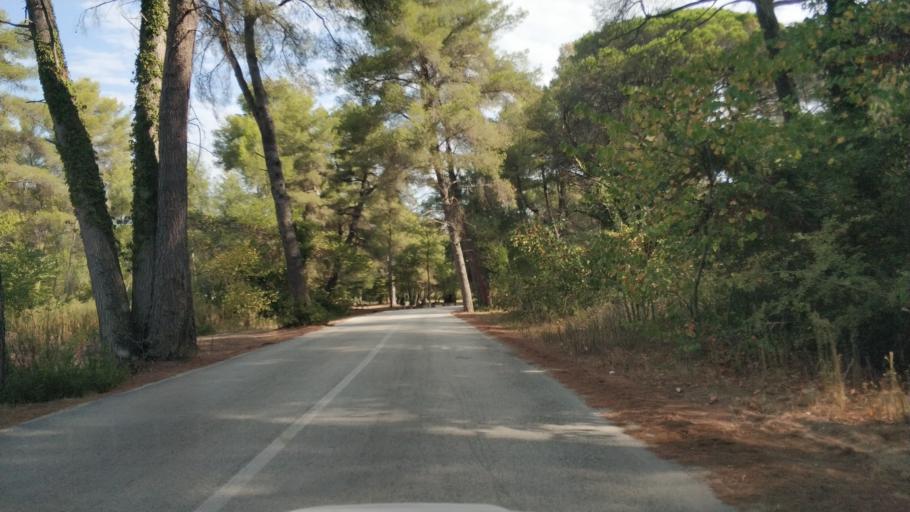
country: AL
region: Fier
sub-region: Rrethi i Lushnjes
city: Divjake
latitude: 40.9885
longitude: 19.4848
